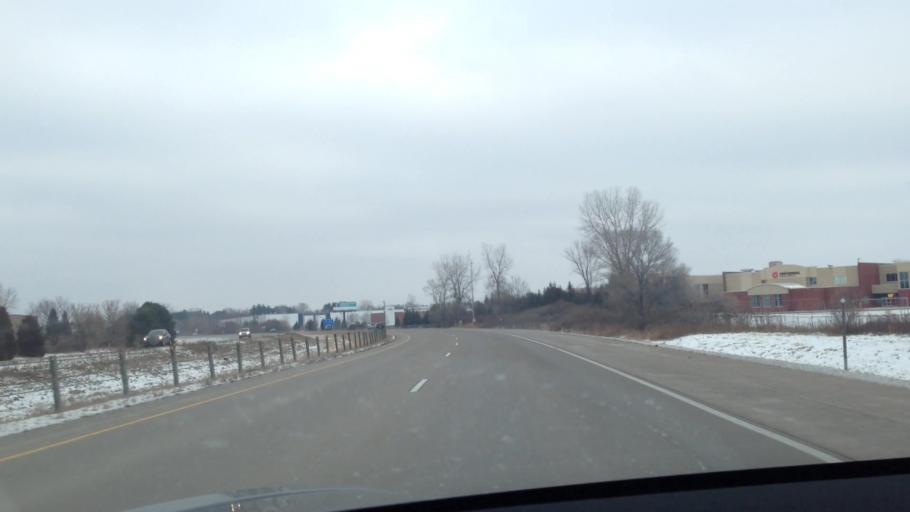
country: US
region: Minnesota
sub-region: Anoka County
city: Circle Pines
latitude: 45.1719
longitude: -93.1271
